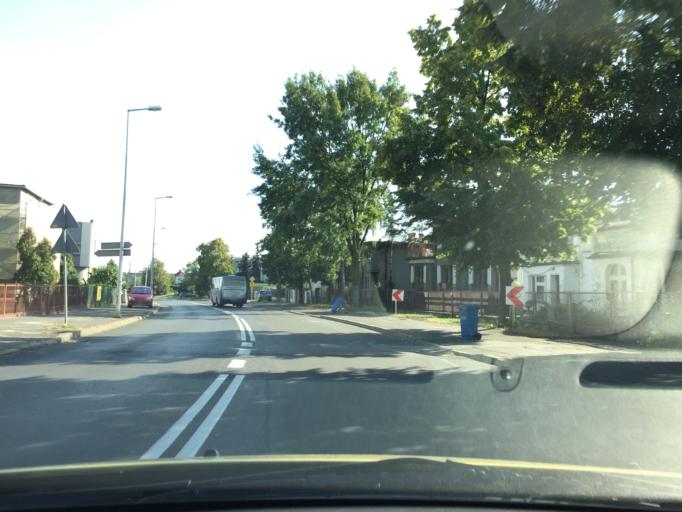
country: PL
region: Greater Poland Voivodeship
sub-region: Kalisz
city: Kalisz
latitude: 51.7758
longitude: 18.0887
